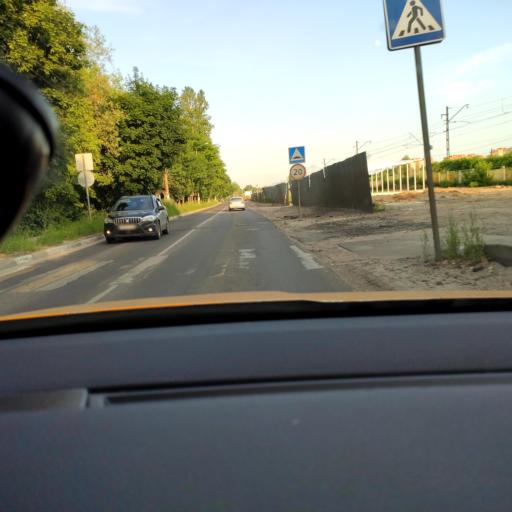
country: RU
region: Moskovskaya
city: Shchelkovo
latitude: 55.9160
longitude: 37.9841
